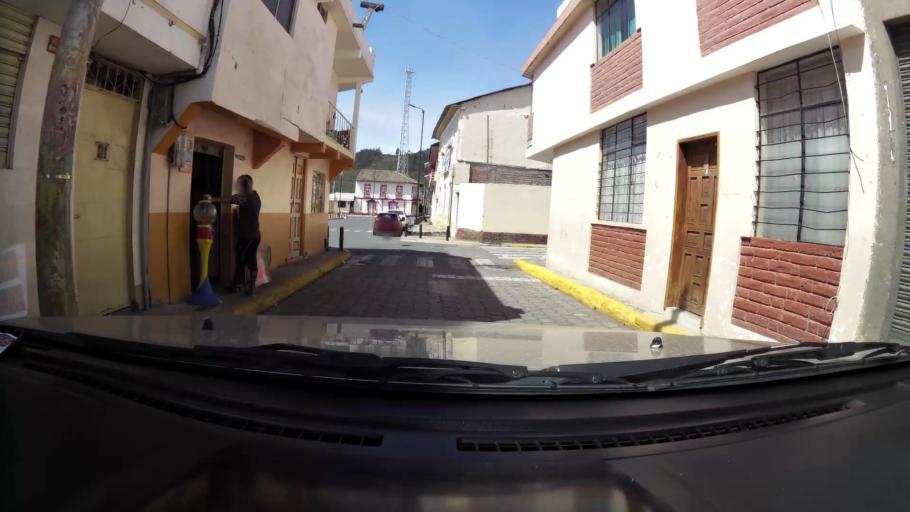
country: EC
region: Chimborazo
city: Guano
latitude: -1.5664
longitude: -78.5313
